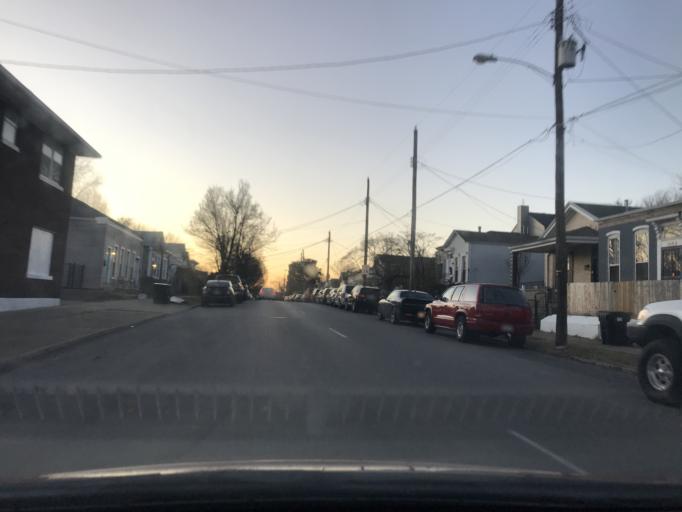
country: US
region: Kentucky
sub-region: Jefferson County
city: Audubon Park
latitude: 38.2336
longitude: -85.7340
